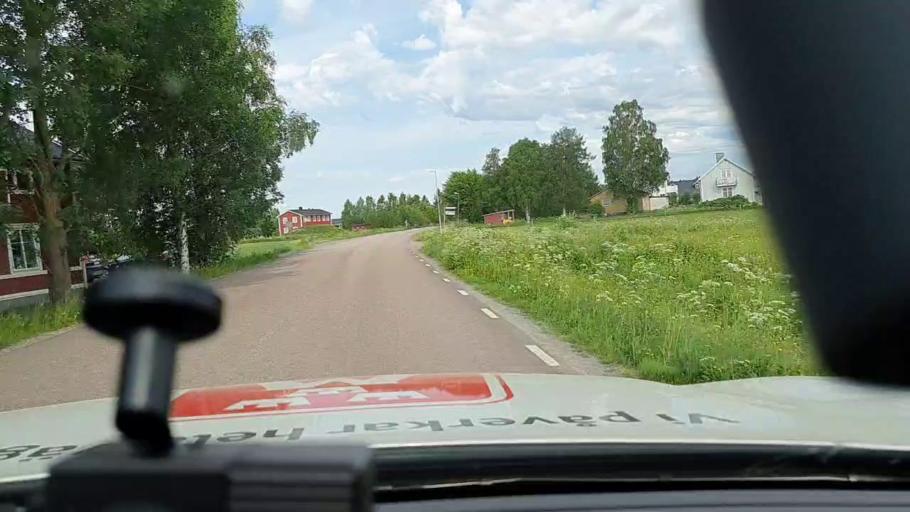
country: SE
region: Norrbotten
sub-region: Bodens Kommun
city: Saevast
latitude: 65.6849
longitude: 21.7898
